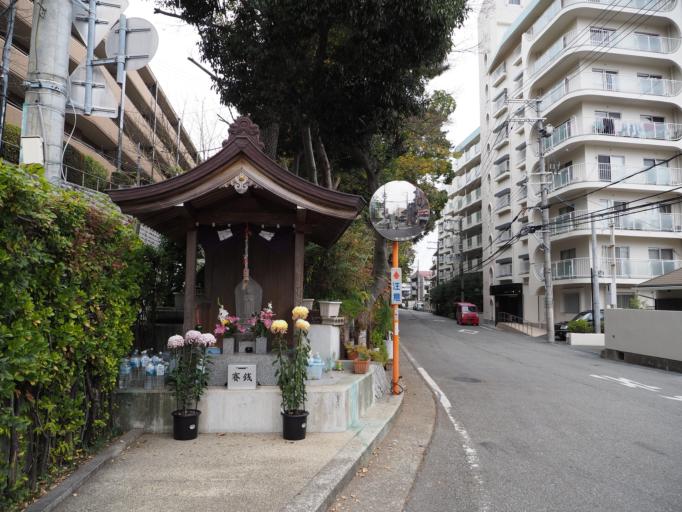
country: JP
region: Hyogo
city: Takarazuka
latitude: 34.7671
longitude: 135.3579
